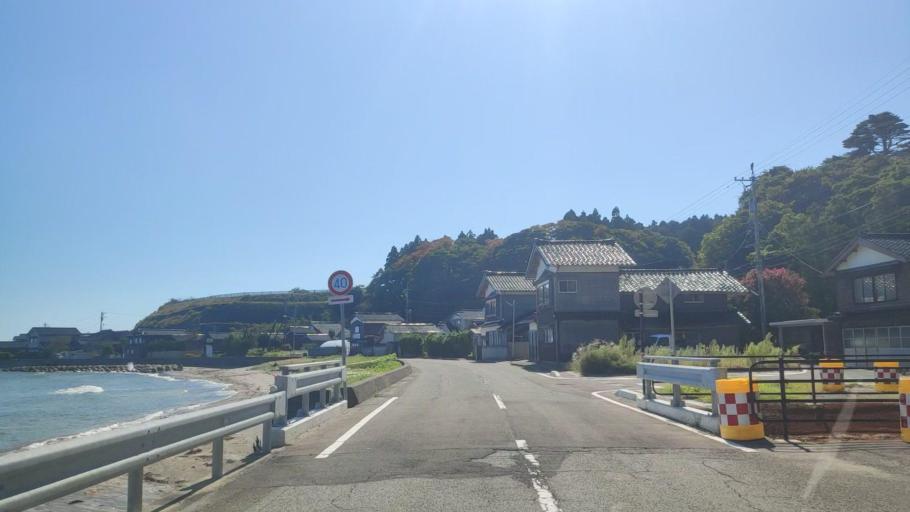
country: JP
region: Toyama
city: Nyuzen
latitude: 37.5004
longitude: 137.3490
